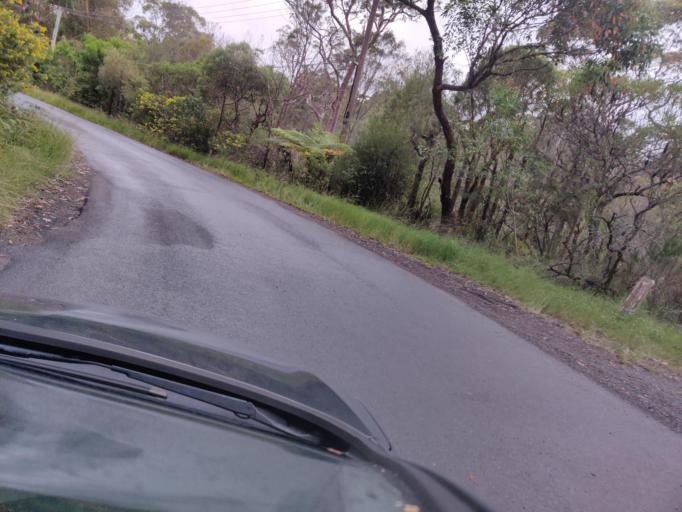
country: AU
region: New South Wales
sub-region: Pittwater
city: Ingleside
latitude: -33.6807
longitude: 151.2536
